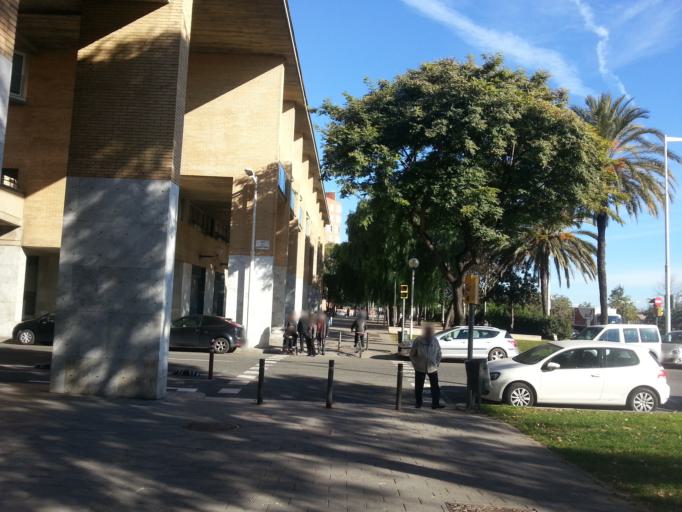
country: ES
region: Catalonia
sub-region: Provincia de Barcelona
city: Sant Marti
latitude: 41.3915
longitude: 2.2002
